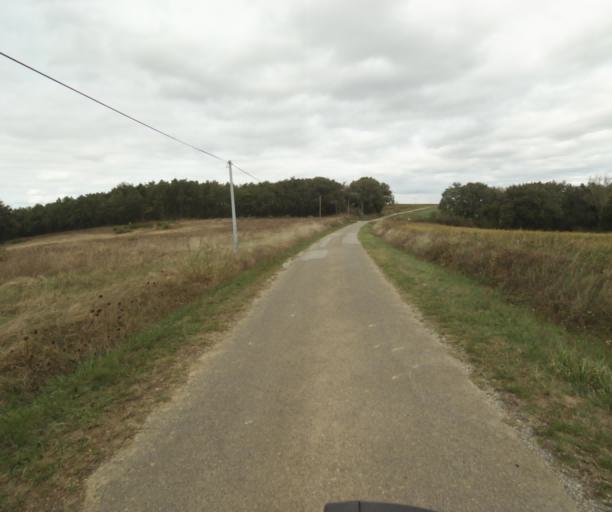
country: FR
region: Midi-Pyrenees
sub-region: Departement du Tarn-et-Garonne
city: Beaumont-de-Lomagne
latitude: 43.8427
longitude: 1.0953
